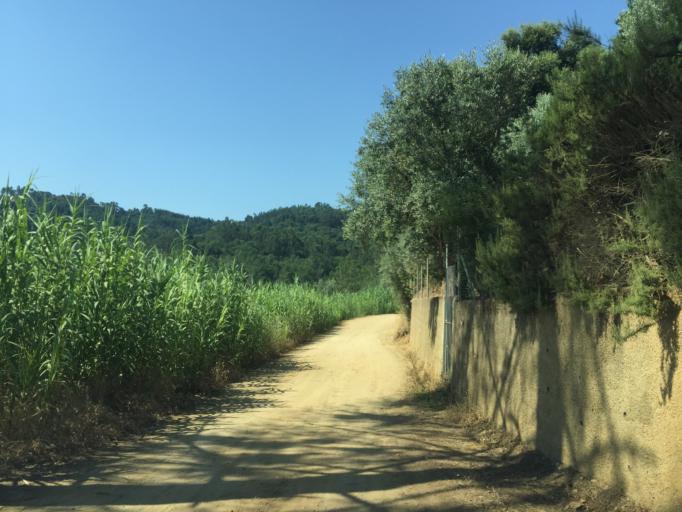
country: PT
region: Santarem
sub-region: Ferreira do Zezere
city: Ferreira do Zezere
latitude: 39.6055
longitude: -8.2763
